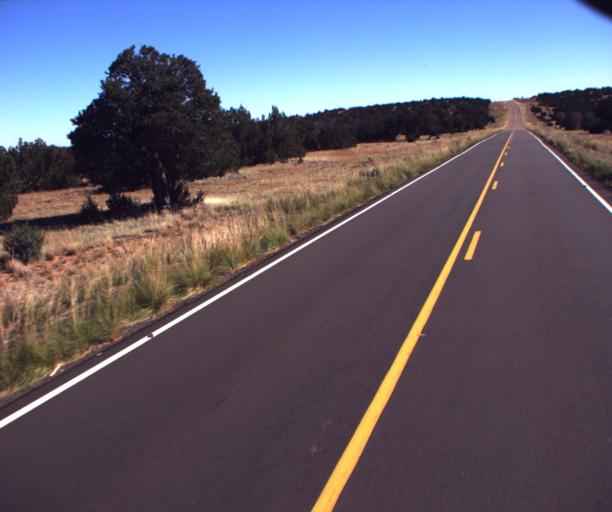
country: US
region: Arizona
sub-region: Navajo County
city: Heber-Overgaard
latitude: 34.4556
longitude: -110.4464
